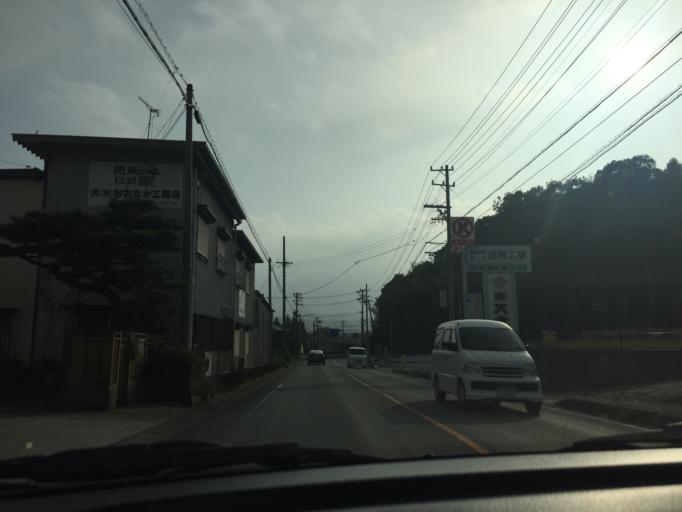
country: JP
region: Aichi
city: Shinshiro
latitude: 34.9269
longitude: 137.5640
